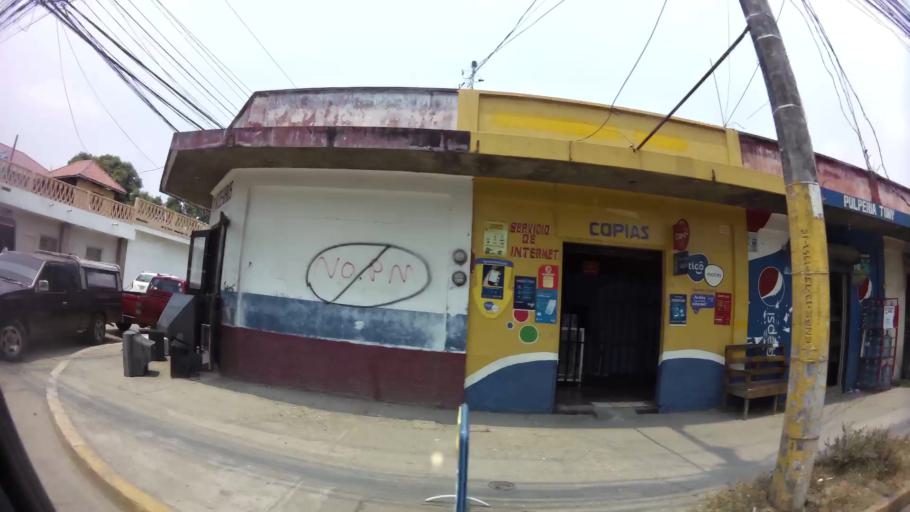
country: HN
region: Yoro
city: El Progreso
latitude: 15.3951
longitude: -87.8081
